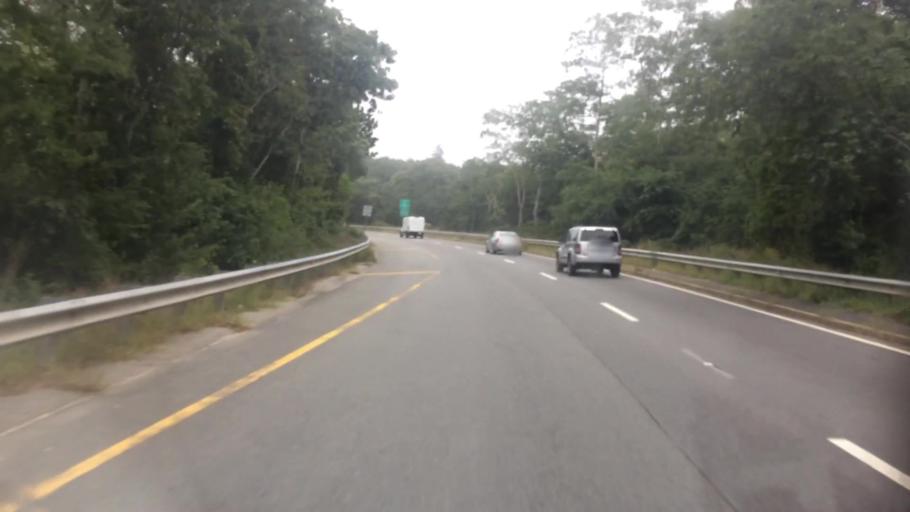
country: US
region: Massachusetts
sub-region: Plymouth County
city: Onset
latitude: 41.7621
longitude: -70.6787
